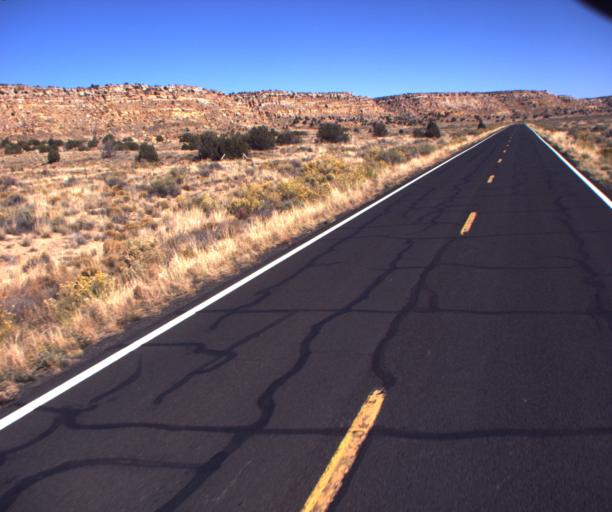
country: US
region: Arizona
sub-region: Navajo County
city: First Mesa
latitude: 35.8363
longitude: -110.2632
